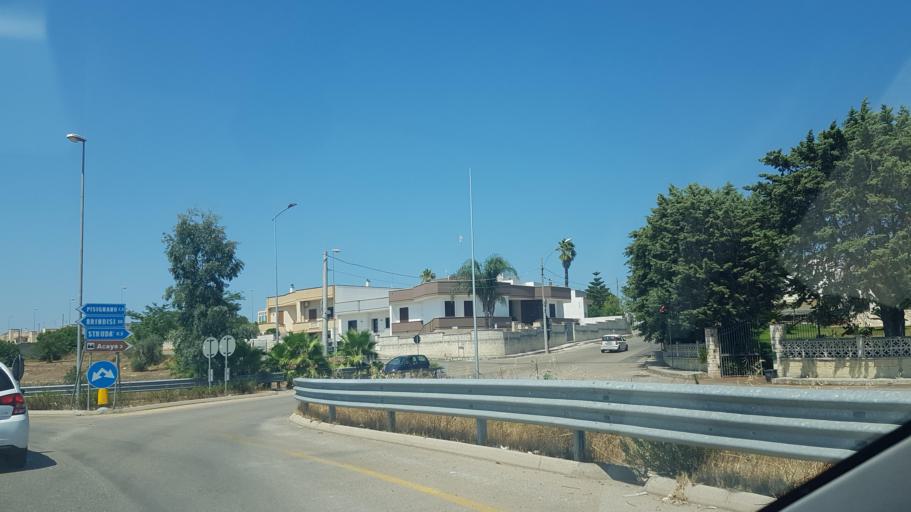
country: IT
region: Apulia
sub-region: Provincia di Lecce
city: Struda
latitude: 40.3152
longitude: 18.2784
